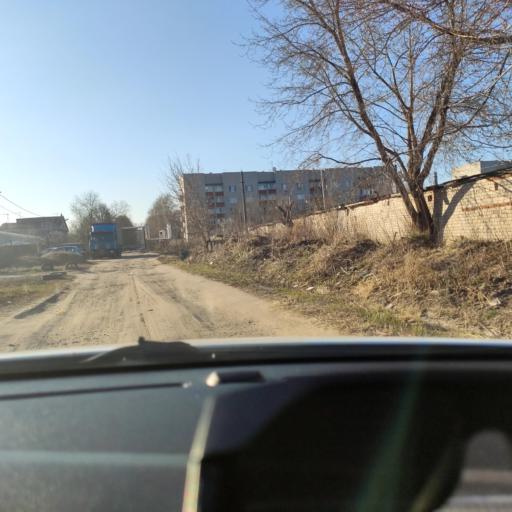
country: RU
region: Tatarstan
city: Vysokaya Gora
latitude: 55.8741
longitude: 49.2374
